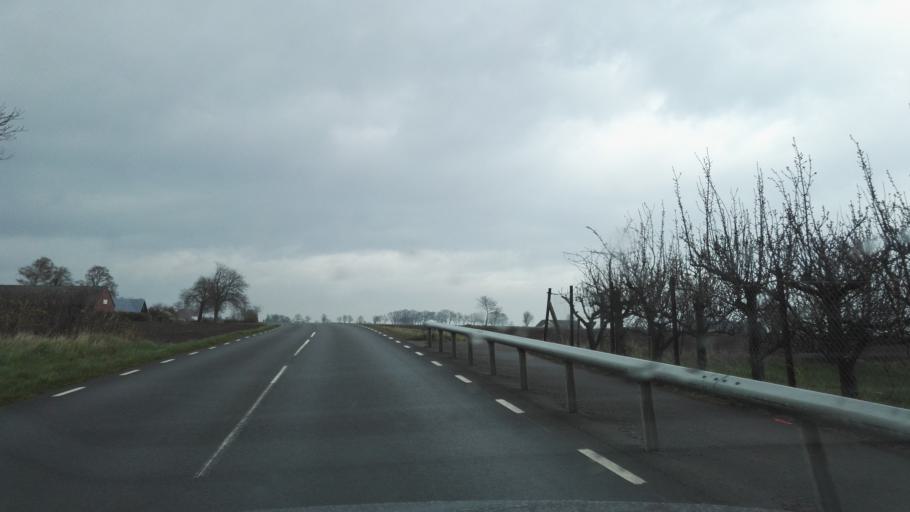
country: SE
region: Skane
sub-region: Simrishamns Kommun
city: Simrishamn
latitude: 55.4869
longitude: 14.2979
